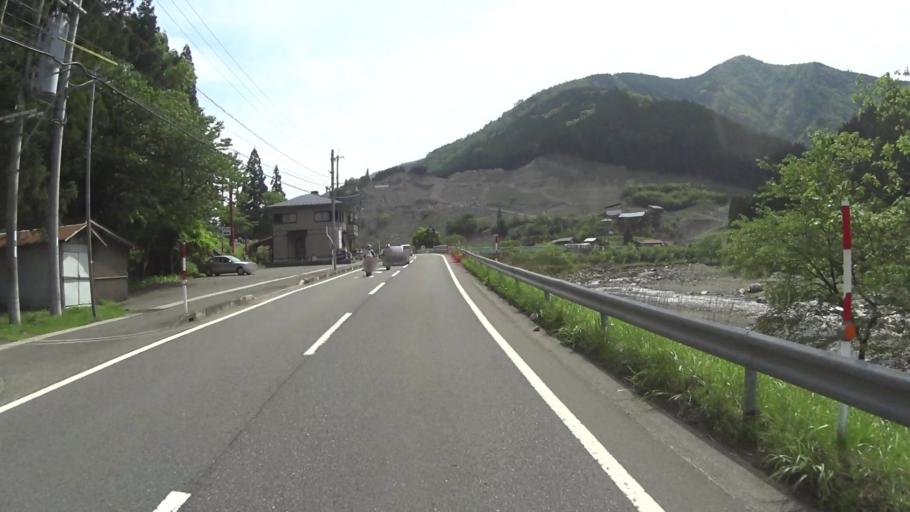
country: JP
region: Shiga Prefecture
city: Kitahama
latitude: 35.2659
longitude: 135.8751
